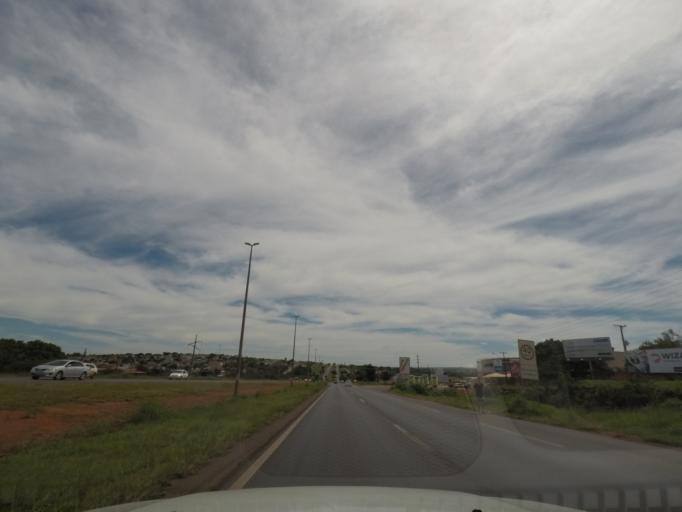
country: BR
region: Goias
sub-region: Planaltina
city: Planaltina
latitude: -15.6100
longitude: -47.6967
